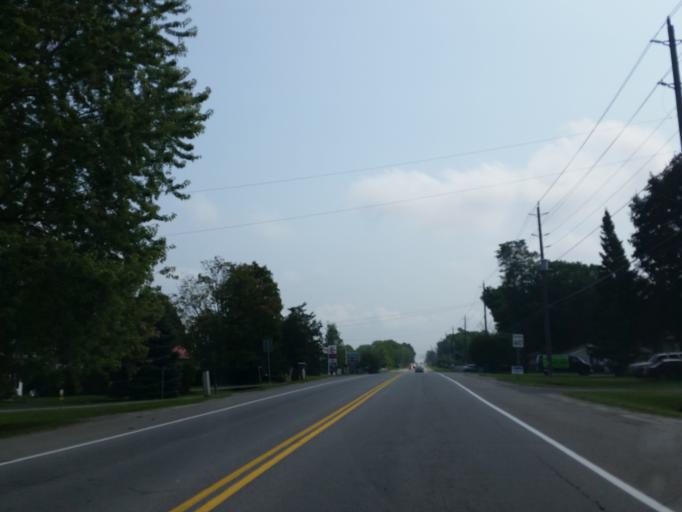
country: CA
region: Ontario
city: Brockville
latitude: 44.6121
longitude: -75.7385
